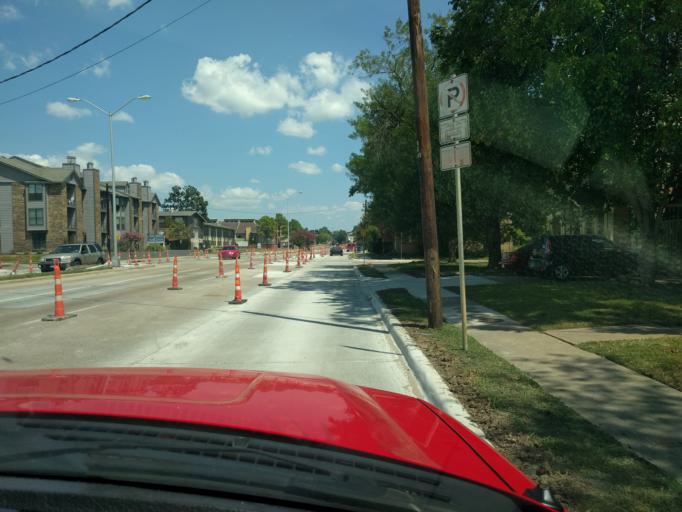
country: US
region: Texas
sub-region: Dallas County
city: Highland Park
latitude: 32.7981
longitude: -96.7599
